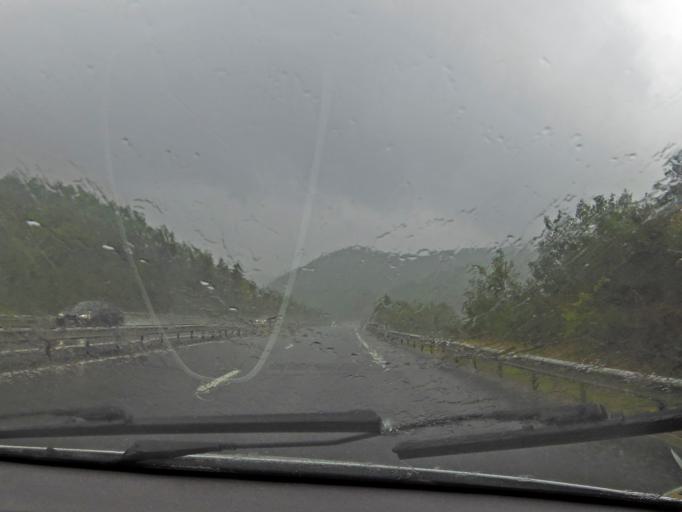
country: FR
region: Auvergne
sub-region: Departement du Cantal
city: Massiac
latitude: 45.2471
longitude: 3.2047
